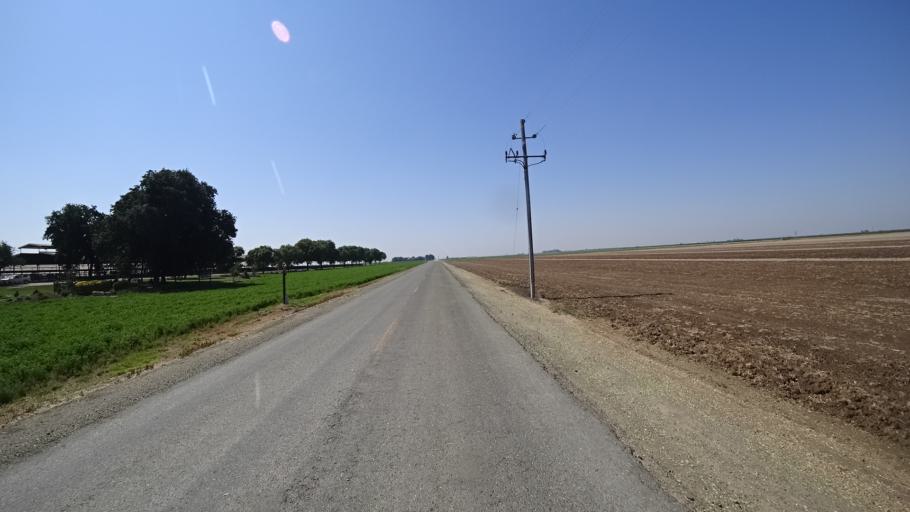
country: US
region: California
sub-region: Tulare County
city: London
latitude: 36.3970
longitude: -119.5289
